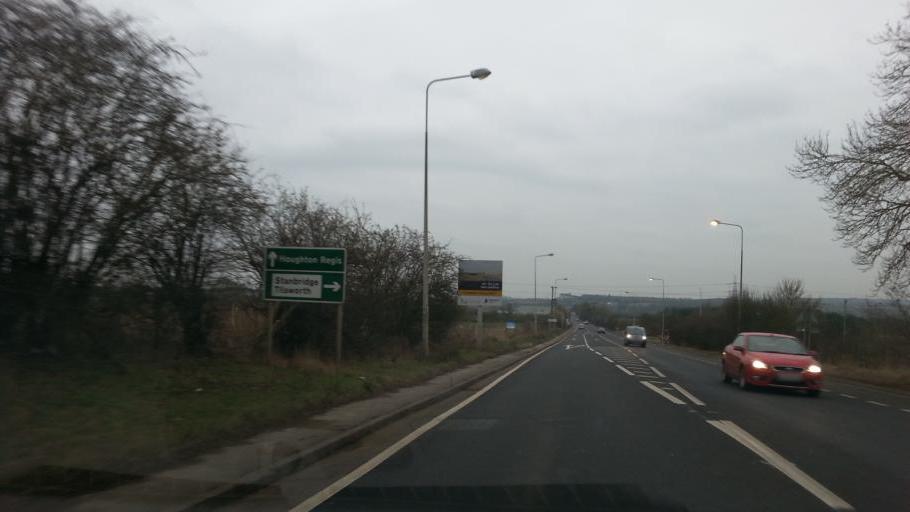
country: GB
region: England
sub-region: Central Bedfordshire
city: Hockliffe
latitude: 51.9168
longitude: -0.5652
